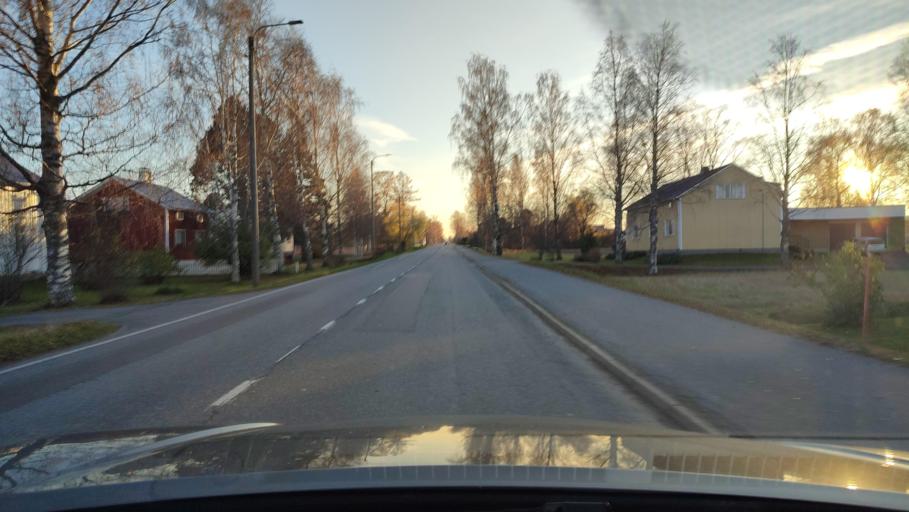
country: FI
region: Ostrobothnia
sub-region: Sydosterbotten
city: Naerpes
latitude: 62.5461
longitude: 21.3978
